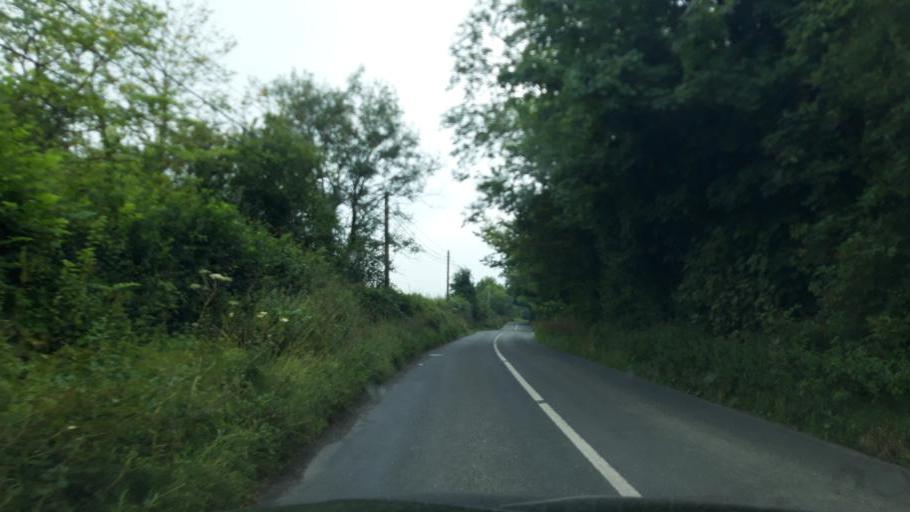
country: IE
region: Munster
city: Fethard
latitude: 52.5341
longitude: -7.6810
